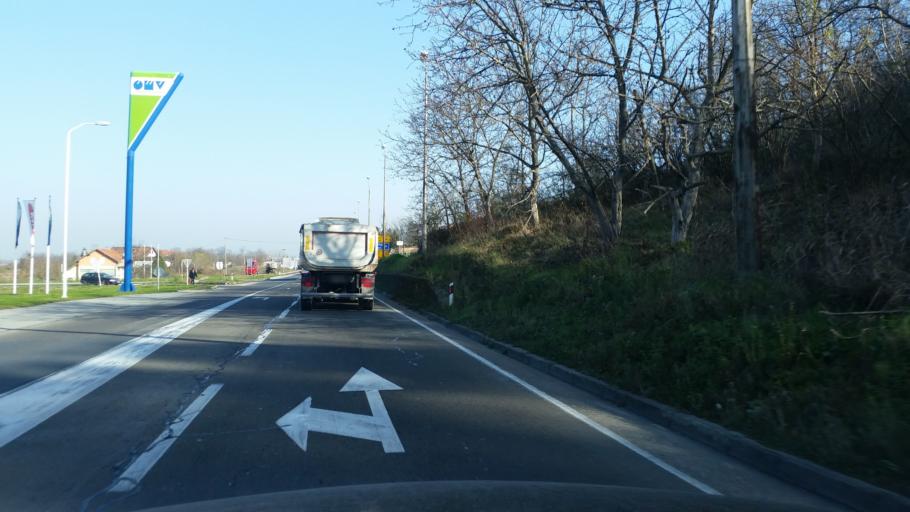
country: RS
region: Central Serbia
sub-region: Kolubarski Okrug
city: Lajkovac
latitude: 44.3649
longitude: 20.1966
